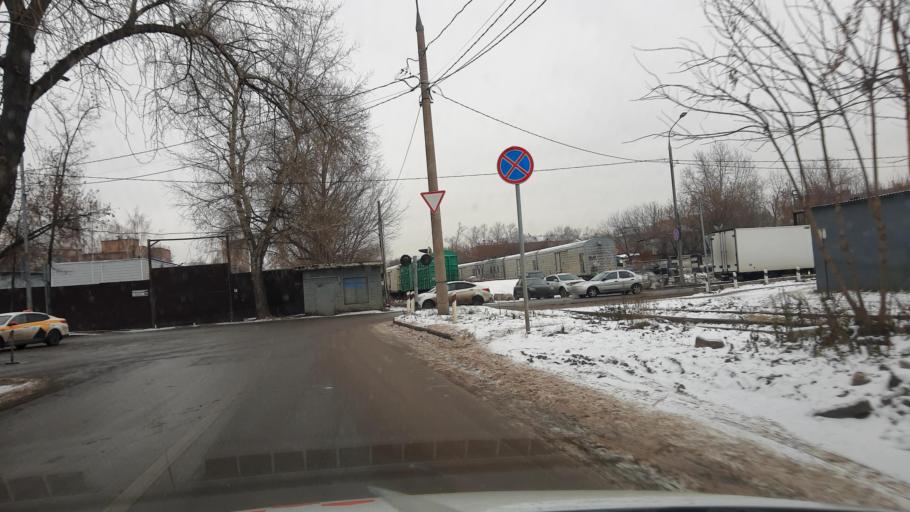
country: RU
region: Moscow
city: Lyublino
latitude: 55.6738
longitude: 37.7357
